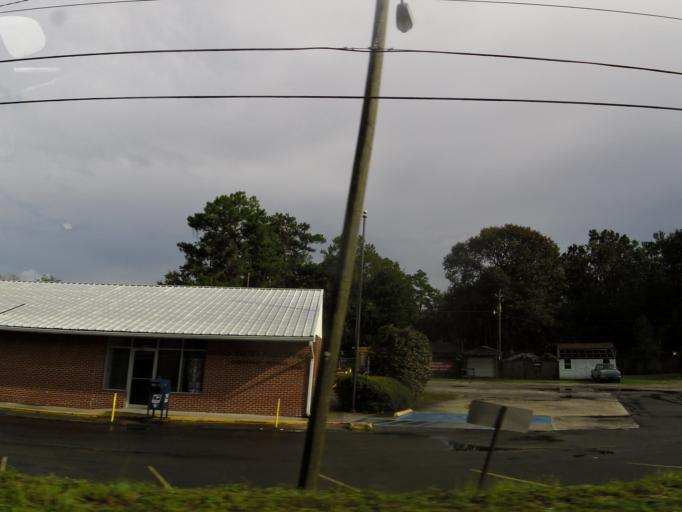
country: US
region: Georgia
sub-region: Liberty County
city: Walthourville
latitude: 31.7859
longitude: -81.6103
